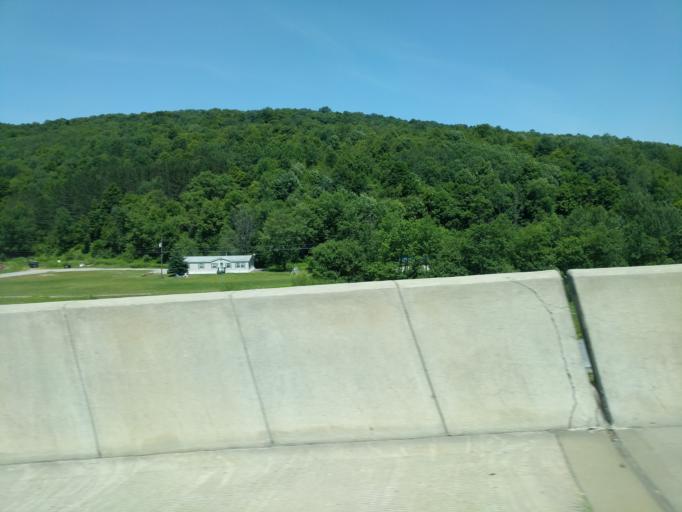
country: US
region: New York
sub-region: Sullivan County
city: Livingston Manor
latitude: 41.8616
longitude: -74.7857
